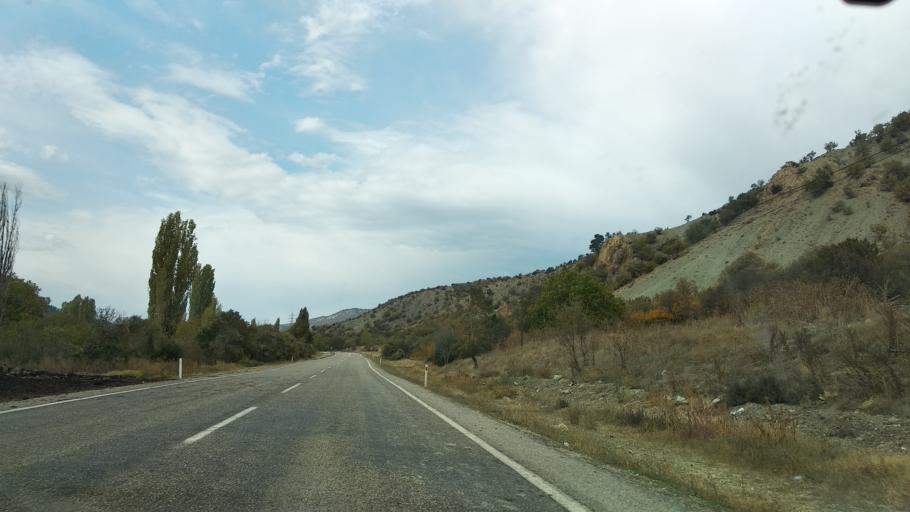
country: TR
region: Ankara
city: Nallihan
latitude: 40.3074
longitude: 31.2909
